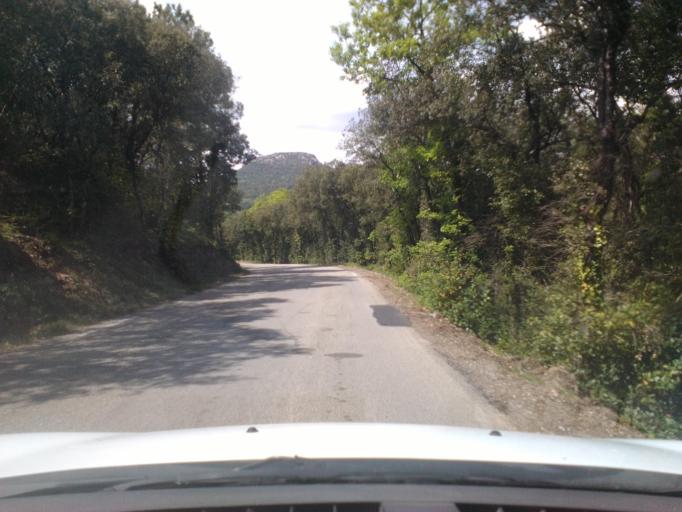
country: FR
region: Languedoc-Roussillon
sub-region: Departement du Gard
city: Saint-Hippolyte-du-Fort
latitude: 43.9796
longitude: 3.8872
